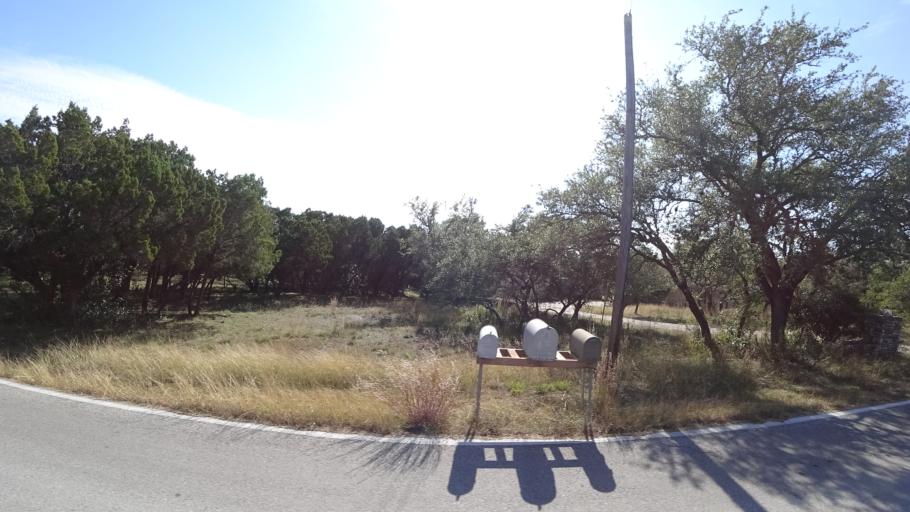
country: US
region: Texas
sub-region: Travis County
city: Barton Creek
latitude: 30.2286
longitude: -97.9105
